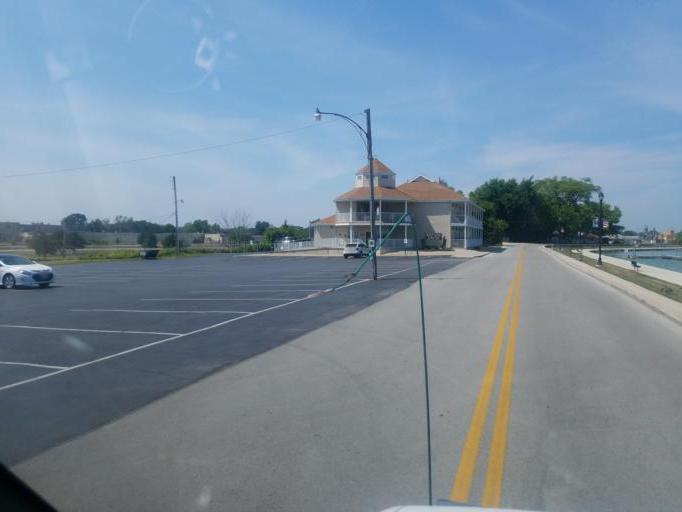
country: US
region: Ohio
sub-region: Mercer County
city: Celina
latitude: 40.5353
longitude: -84.5743
